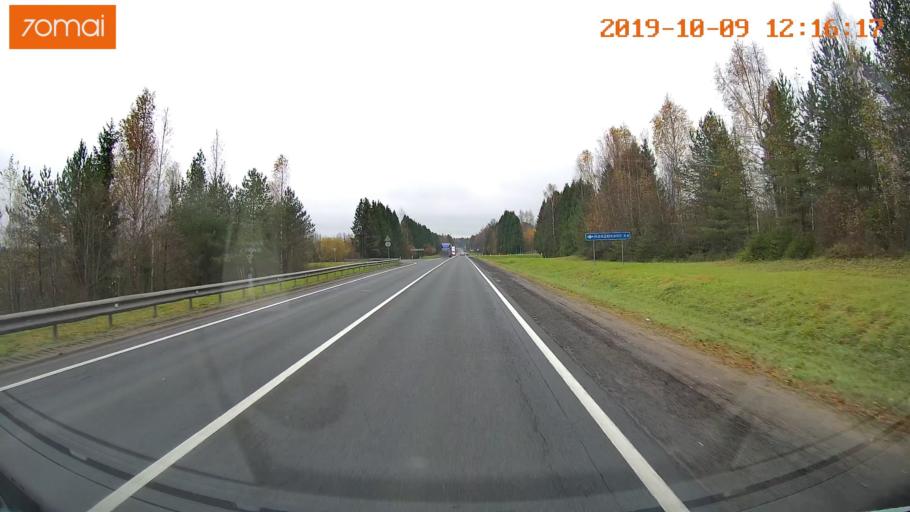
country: RU
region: Jaroslavl
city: Prechistoye
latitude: 58.4707
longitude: 40.3214
